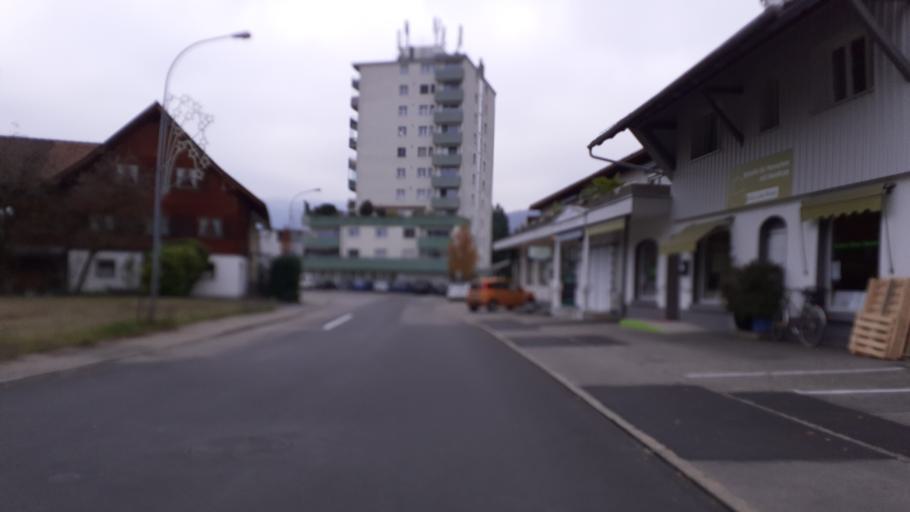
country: AT
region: Vorarlberg
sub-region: Politischer Bezirk Dornbirn
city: Lustenau
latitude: 47.4274
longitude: 9.6556
